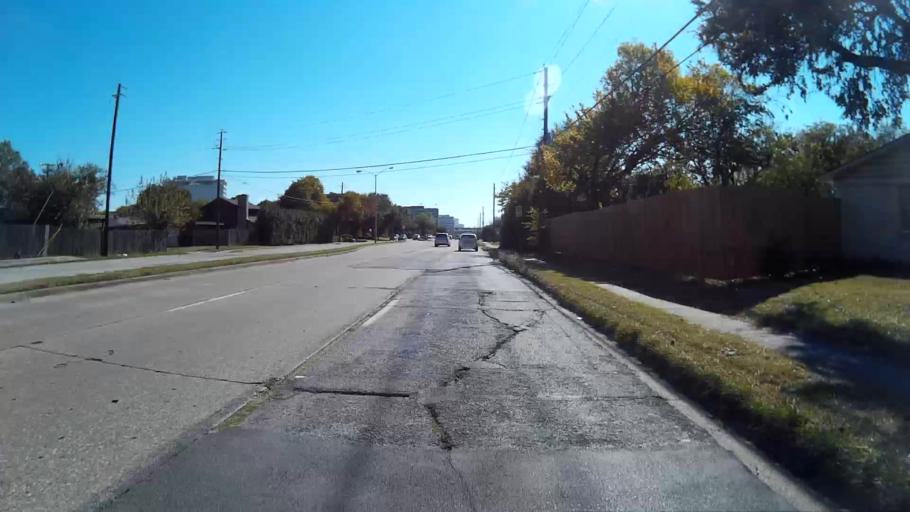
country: US
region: Texas
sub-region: Dallas County
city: Richardson
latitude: 32.9293
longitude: -96.7691
